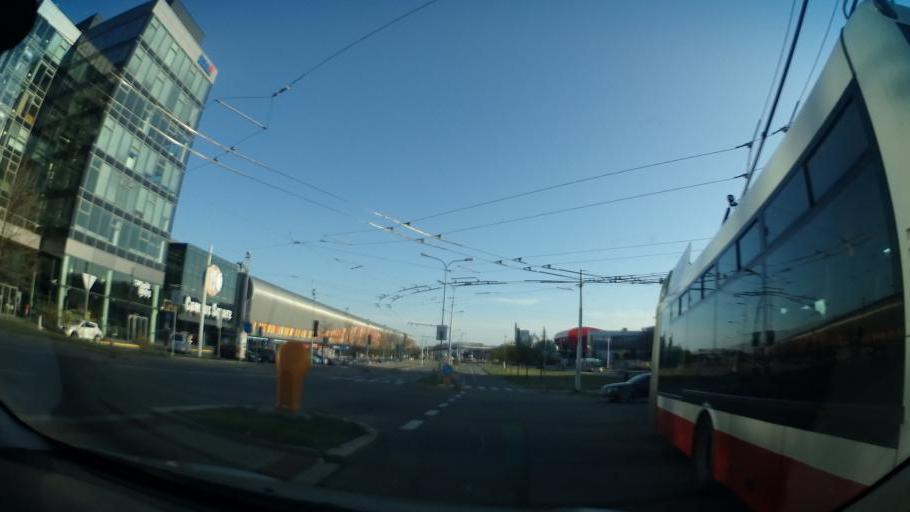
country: CZ
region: South Moravian
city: Ostopovice
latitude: 49.1753
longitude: 16.5671
